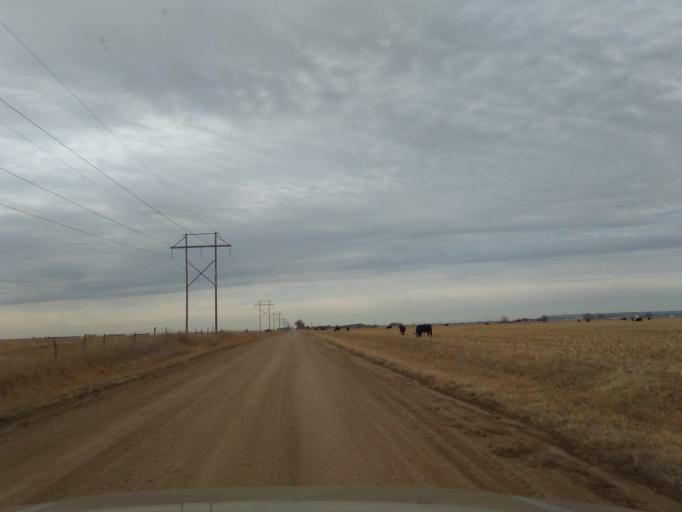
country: US
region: Nebraska
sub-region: Buffalo County
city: Shelton
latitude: 40.6548
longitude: -98.7390
